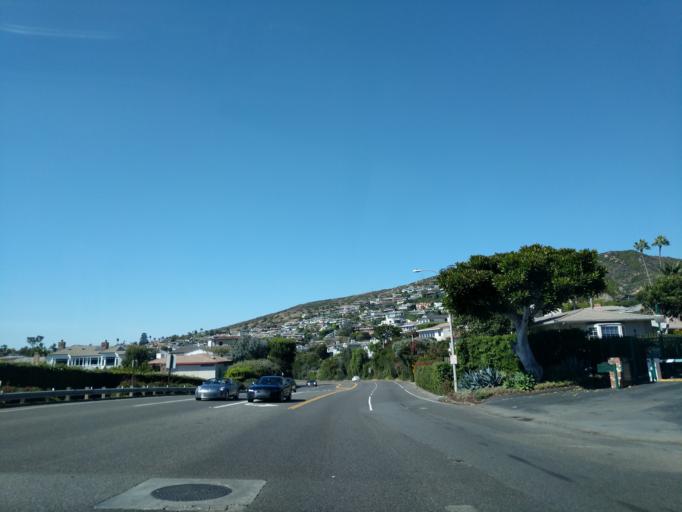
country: US
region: California
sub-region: Orange County
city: Laguna Beach
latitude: 33.5508
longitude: -117.8051
